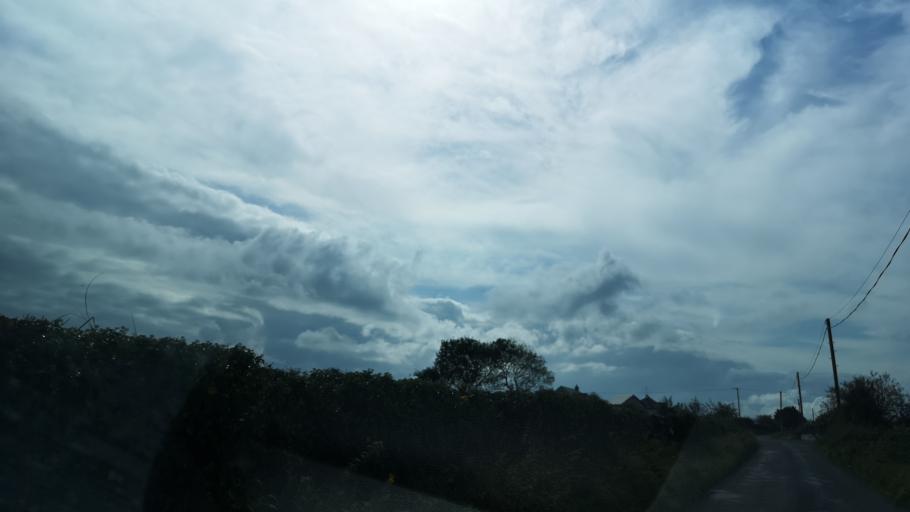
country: IE
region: Connaught
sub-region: County Galway
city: Athenry
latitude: 53.3107
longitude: -8.8075
